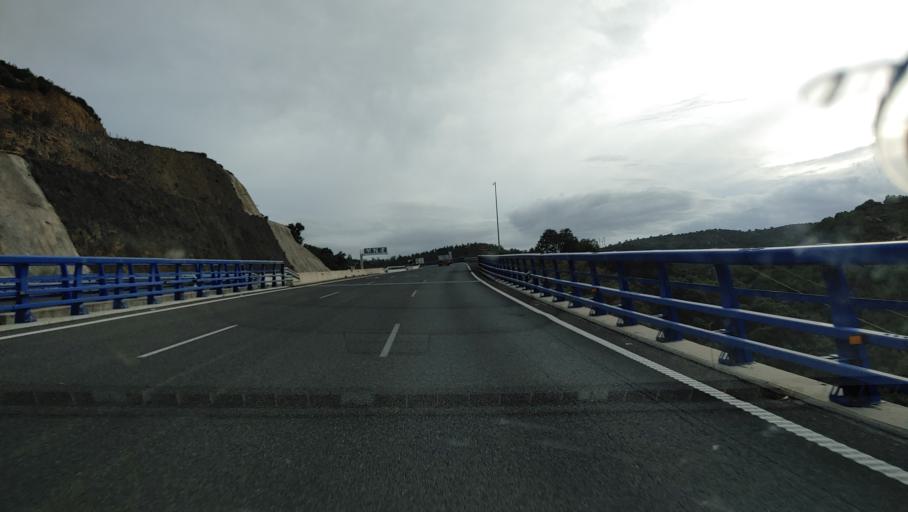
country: ES
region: Andalusia
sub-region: Provincia de Jaen
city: Santa Elena
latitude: 38.3595
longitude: -3.5257
